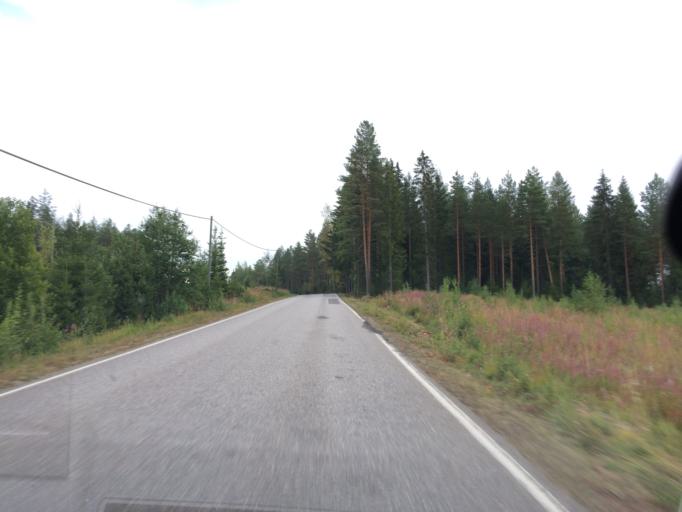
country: FI
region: Haeme
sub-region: Haemeenlinna
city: Tuulos
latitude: 61.1942
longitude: 24.7432
